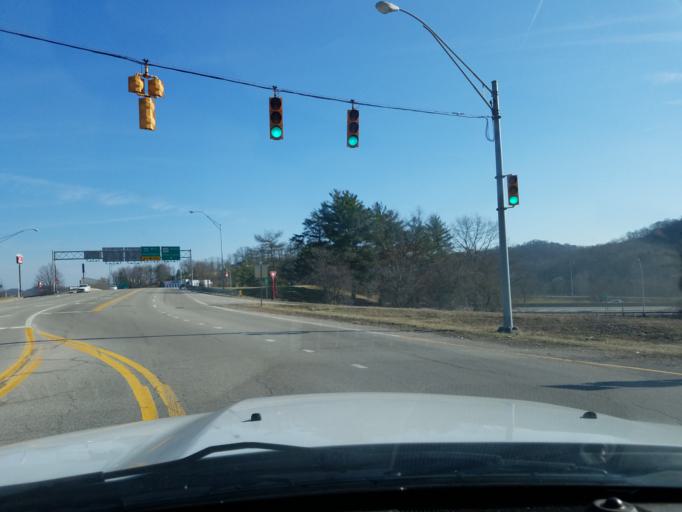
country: US
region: West Virginia
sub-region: Kanawha County
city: Cross Lanes
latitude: 38.4123
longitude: -81.7977
